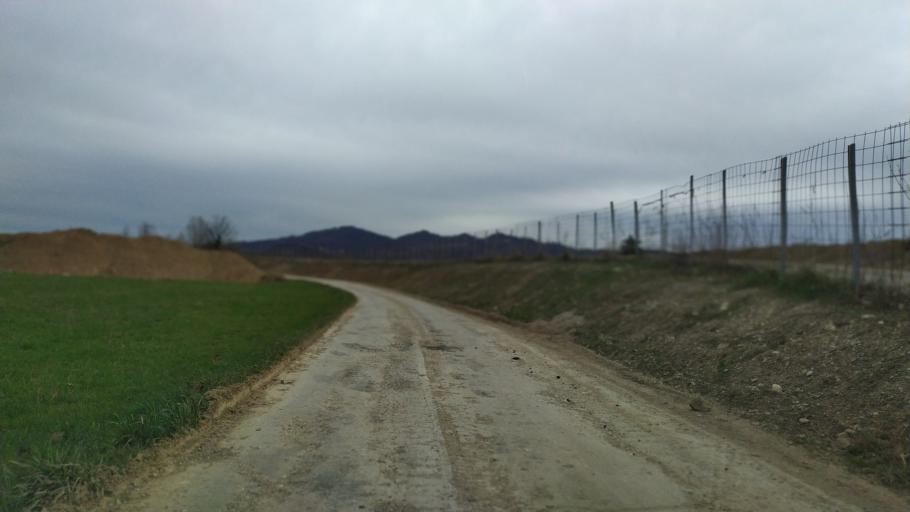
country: IT
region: Veneto
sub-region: Provincia di Vicenza
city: Malo
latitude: 45.6547
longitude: 11.4353
